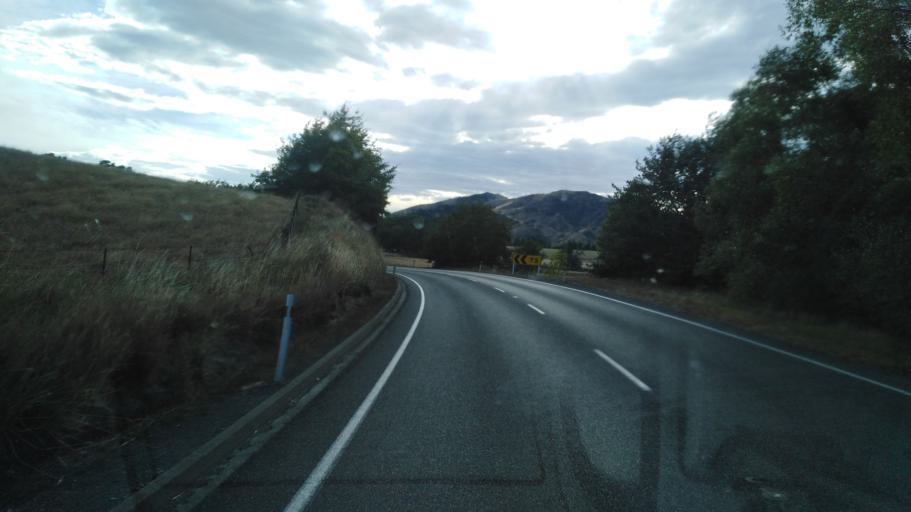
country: NZ
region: Canterbury
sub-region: Hurunui District
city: Amberley
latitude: -42.9354
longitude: 173.0626
